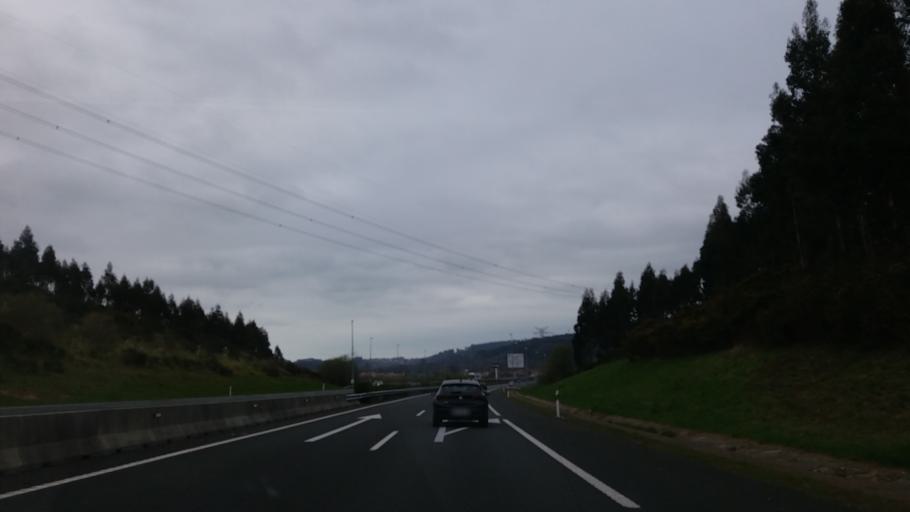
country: ES
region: Cantabria
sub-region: Provincia de Cantabria
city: Luzmela
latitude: 43.3234
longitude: -4.2020
